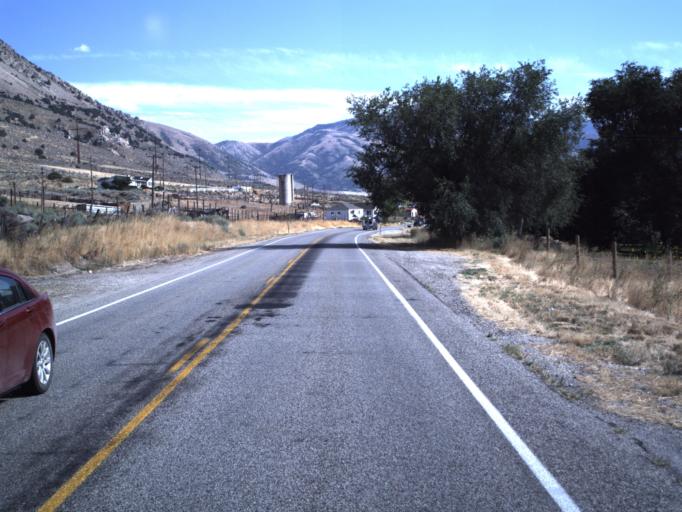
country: US
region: Utah
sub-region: Box Elder County
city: Brigham City
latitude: 41.5469
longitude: -112.0162
